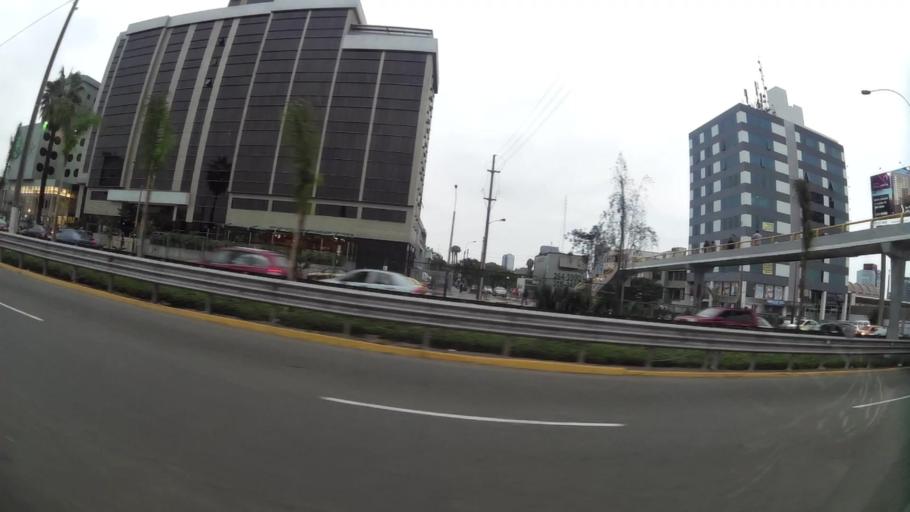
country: PE
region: Lima
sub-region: Lima
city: San Luis
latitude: -12.0902
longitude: -77.0191
